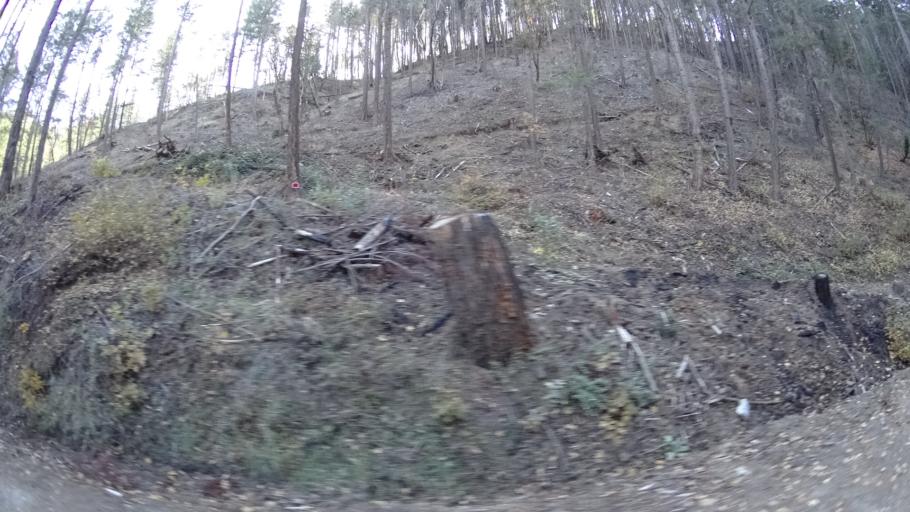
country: US
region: California
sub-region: Siskiyou County
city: Yreka
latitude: 41.8308
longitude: -122.9511
